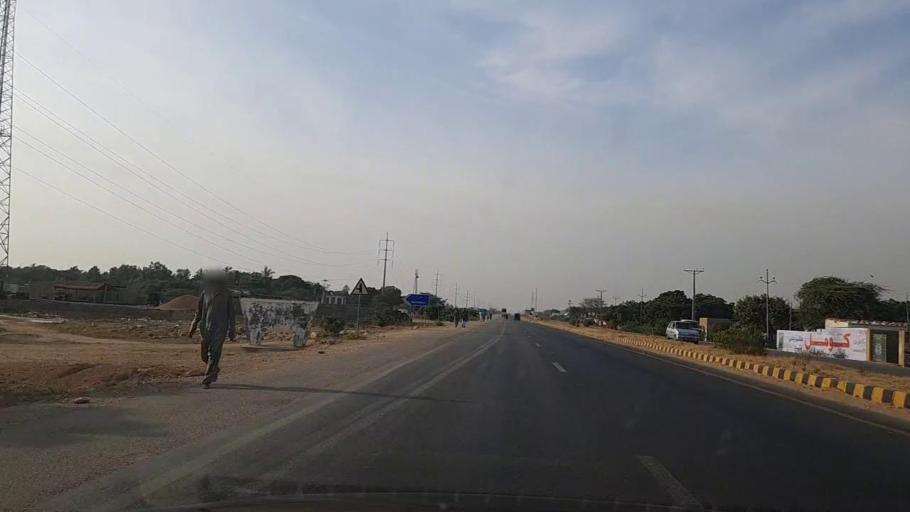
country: PK
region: Sindh
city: Gharo
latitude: 24.7802
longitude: 67.5369
